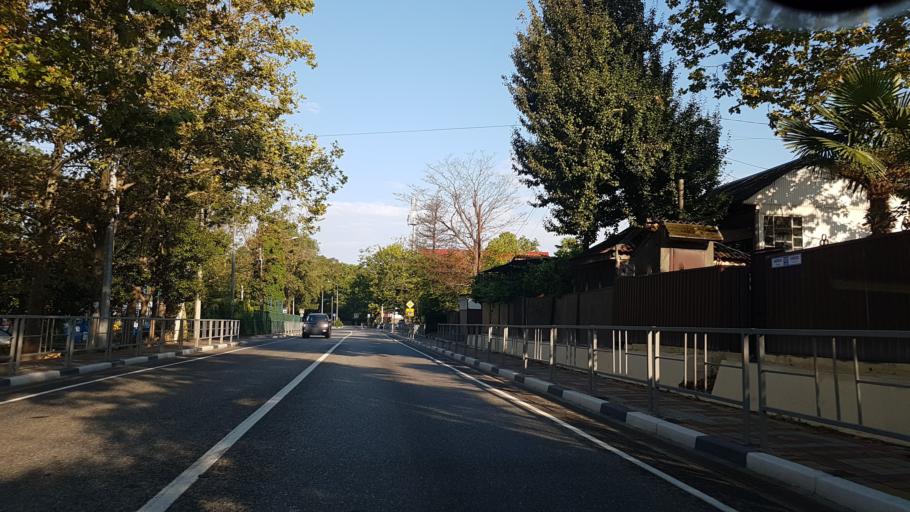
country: RU
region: Krasnodarskiy
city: Vardane
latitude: 43.7286
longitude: 39.5613
